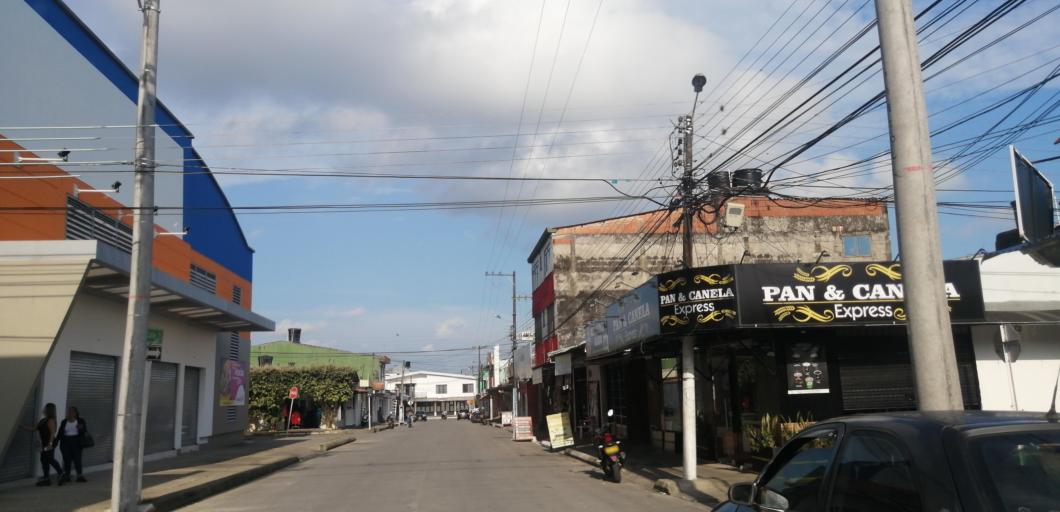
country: CO
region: Meta
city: Acacias
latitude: 3.9855
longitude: -73.7760
